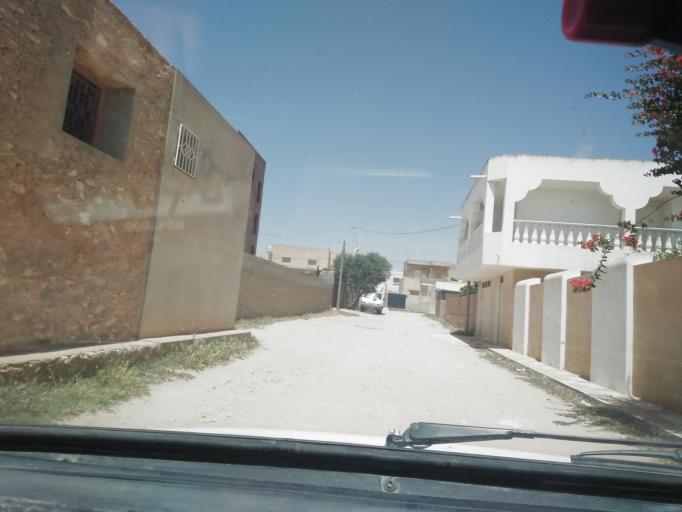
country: TN
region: Safaqis
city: Al Qarmadah
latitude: 34.8070
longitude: 10.7725
